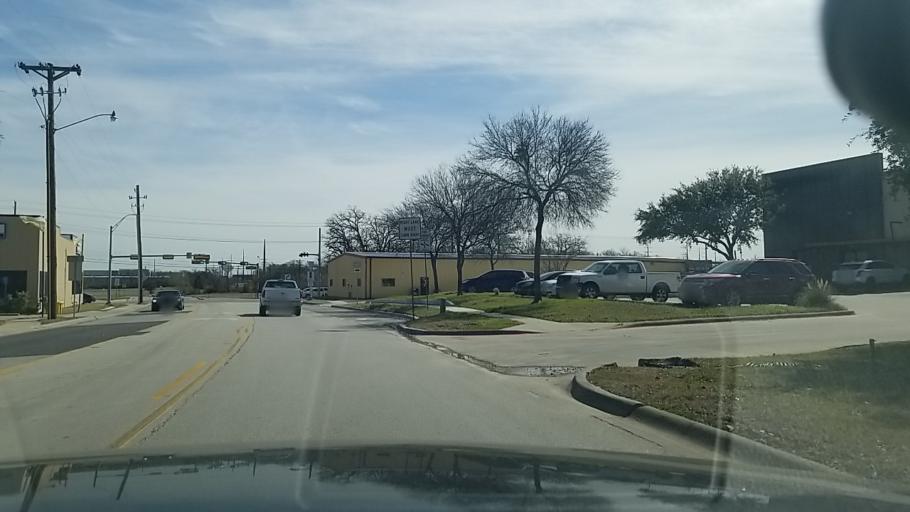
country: US
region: Texas
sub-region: Denton County
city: Denton
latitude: 33.2015
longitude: -97.1135
